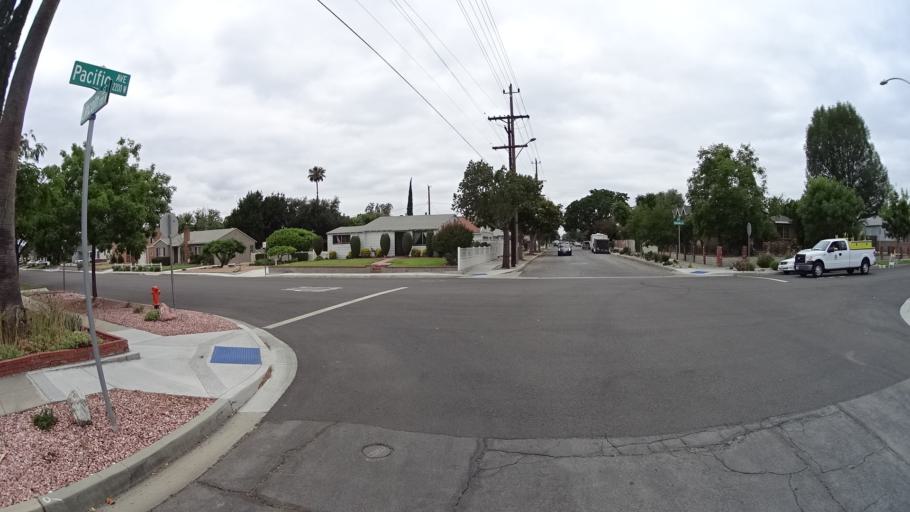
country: US
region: California
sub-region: Los Angeles County
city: Burbank
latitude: 34.1882
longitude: -118.3358
